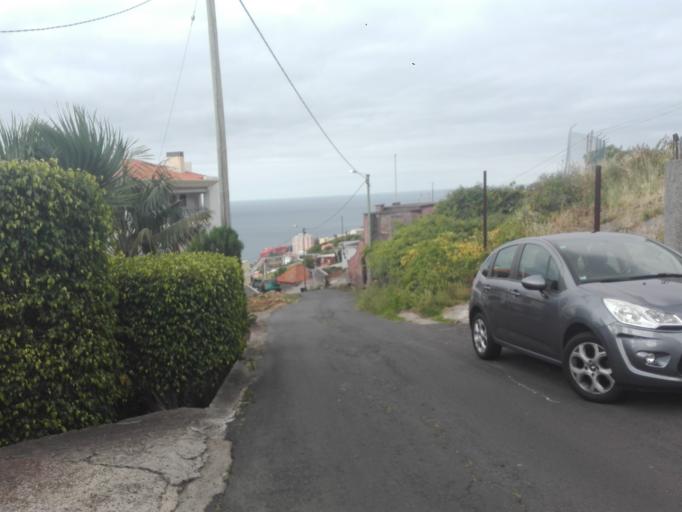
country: PT
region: Madeira
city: Canico
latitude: 32.6519
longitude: -16.8268
